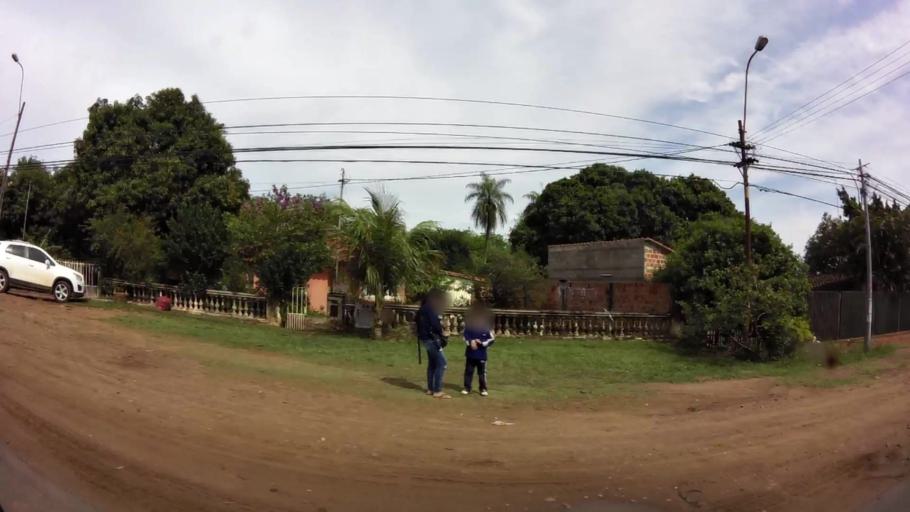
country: PY
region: Central
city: Limpio
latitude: -25.1614
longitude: -57.4755
